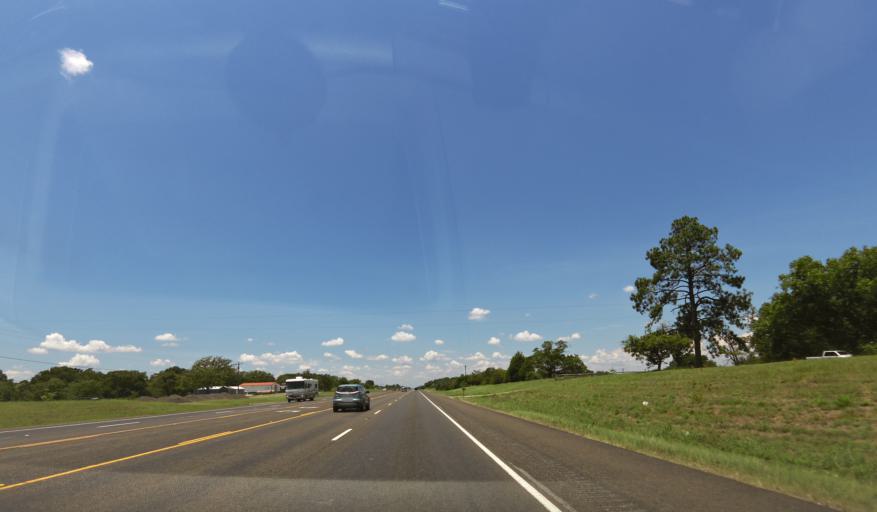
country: US
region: Texas
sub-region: Washington County
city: Brenham
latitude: 30.1708
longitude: -96.4444
